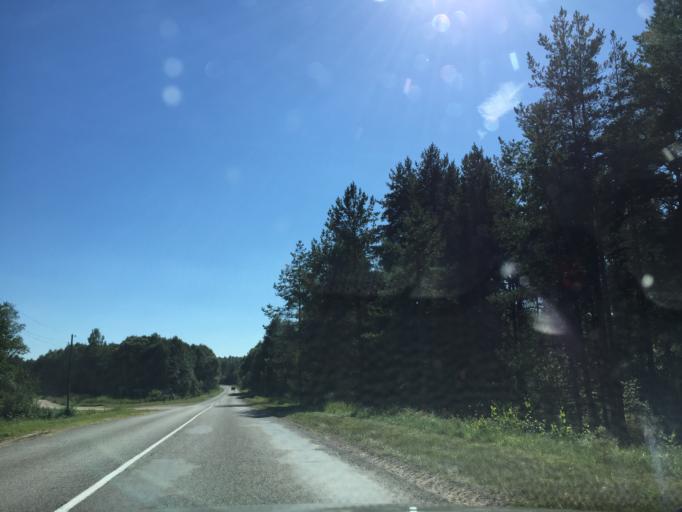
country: LV
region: Akniste
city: Akniste
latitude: 56.1257
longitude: 25.8311
